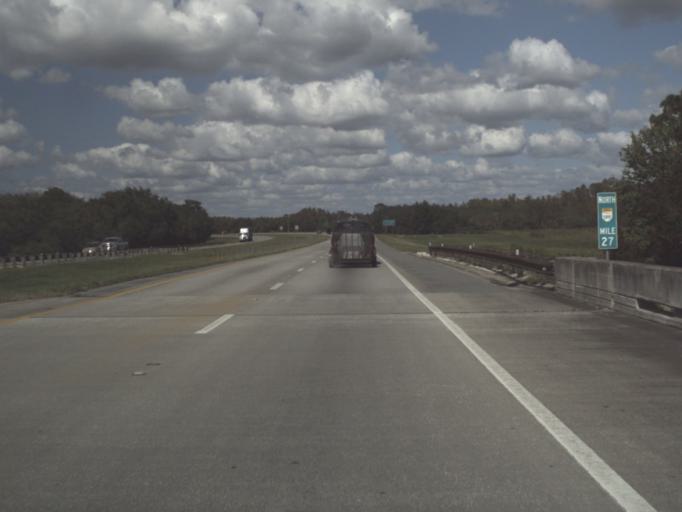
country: US
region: Florida
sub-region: Pasco County
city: Shady Hills
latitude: 28.3097
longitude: -82.5502
